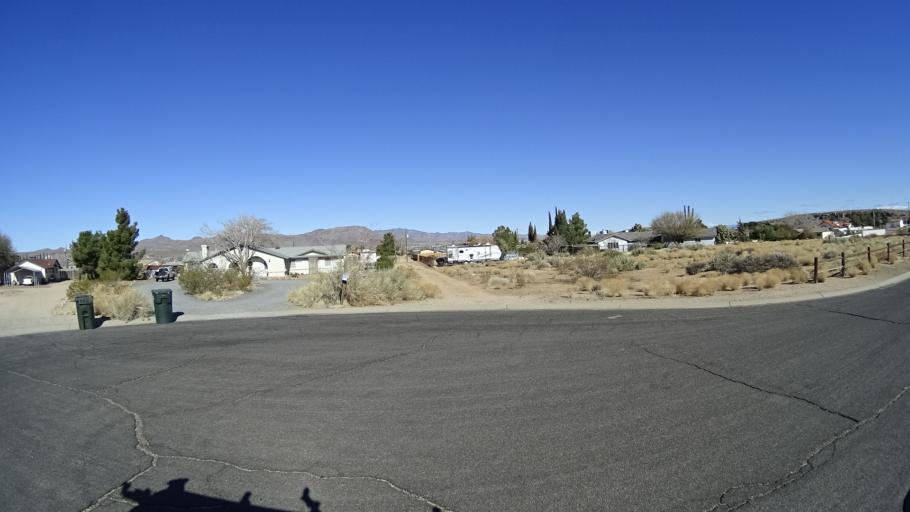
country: US
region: Arizona
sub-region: Mohave County
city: Kingman
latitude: 35.2007
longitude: -114.0091
